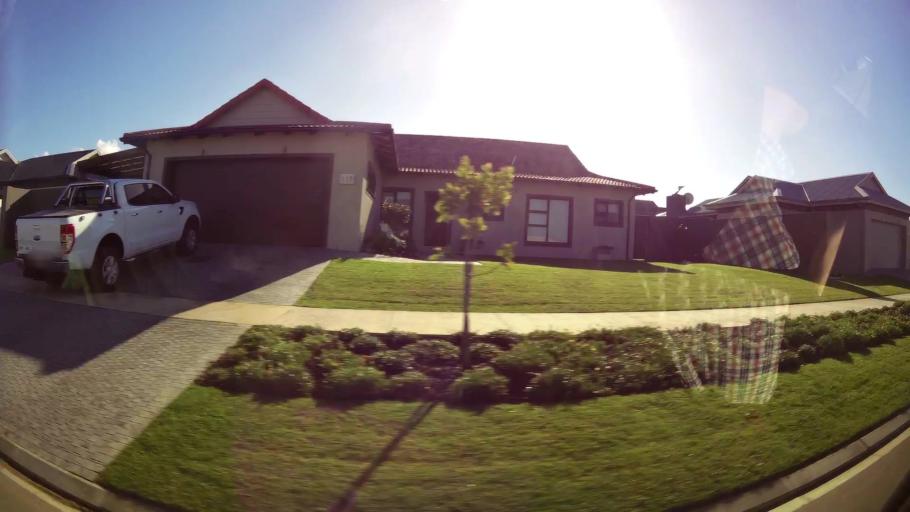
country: ZA
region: Western Cape
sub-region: Eden District Municipality
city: George
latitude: -33.9615
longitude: 22.4196
